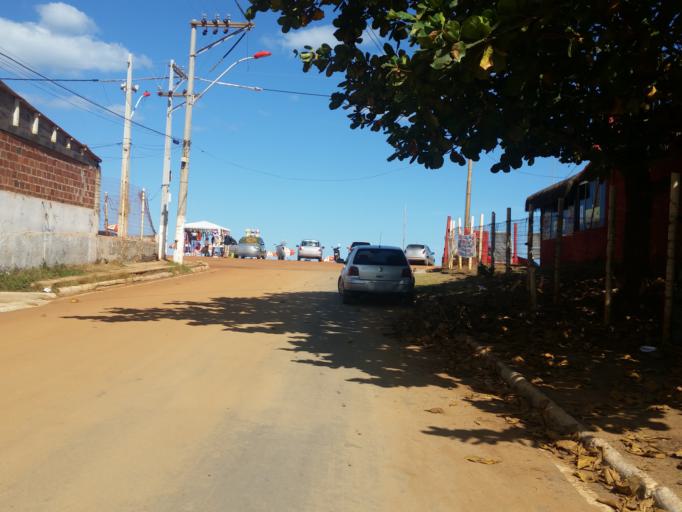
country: BR
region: Rio de Janeiro
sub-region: Marica
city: Marica
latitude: -22.9694
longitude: -42.9622
